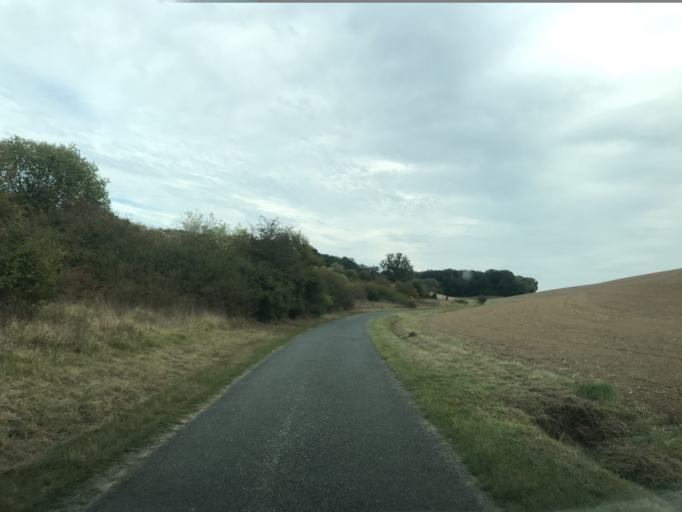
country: FR
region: Haute-Normandie
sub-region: Departement de l'Eure
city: Heudreville-sur-Eure
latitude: 49.0879
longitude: 1.2265
